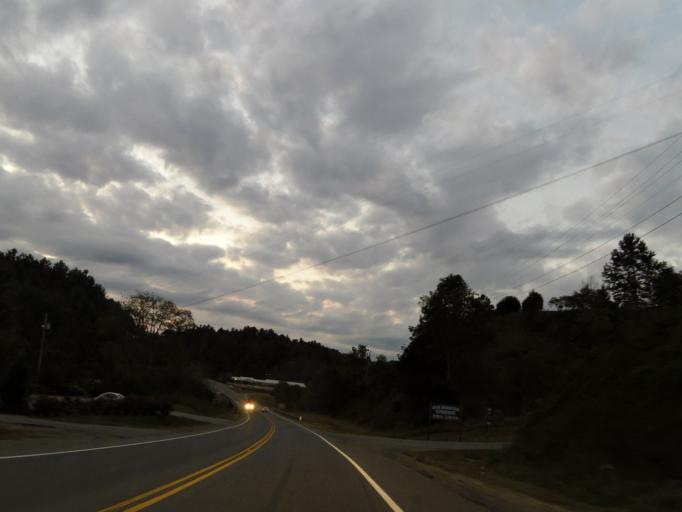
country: US
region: North Carolina
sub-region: Madison County
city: Marshall
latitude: 35.8014
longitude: -82.6566
